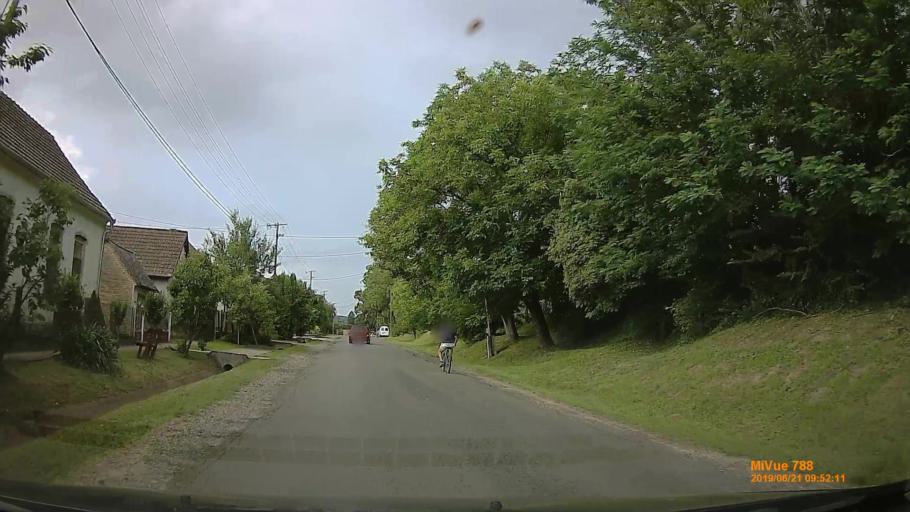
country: HU
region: Baranya
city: Sasd
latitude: 46.2452
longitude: 18.0173
